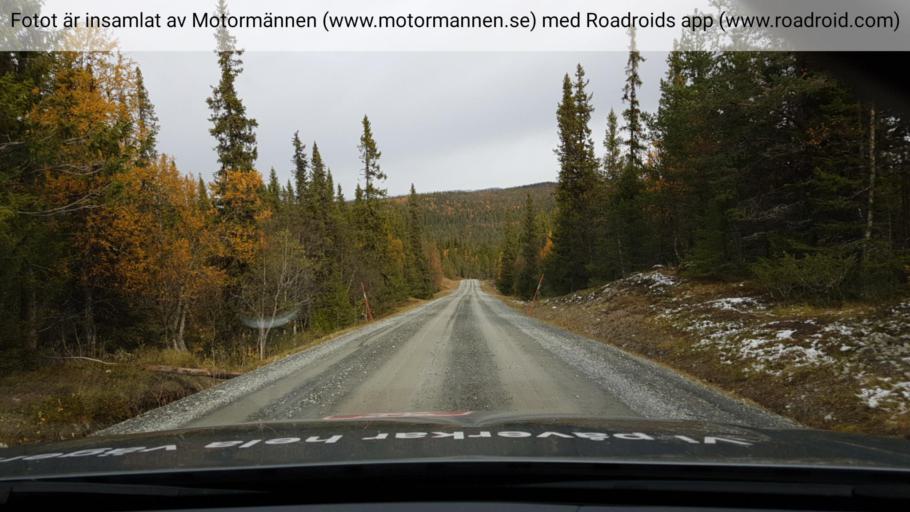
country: SE
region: Jaemtland
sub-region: Are Kommun
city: Are
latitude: 62.7966
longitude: 12.7617
